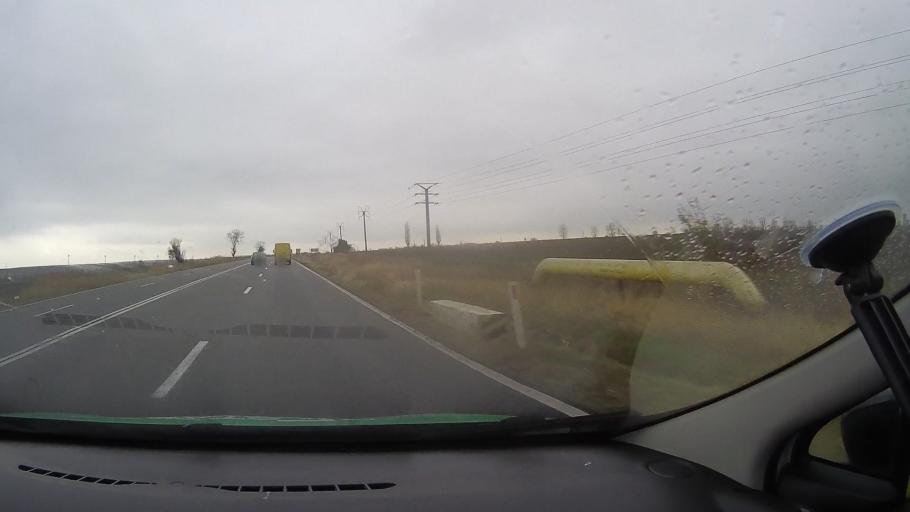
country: RO
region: Constanta
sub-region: Comuna Cumpana
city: Cumpana
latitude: 44.1660
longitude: 28.5347
